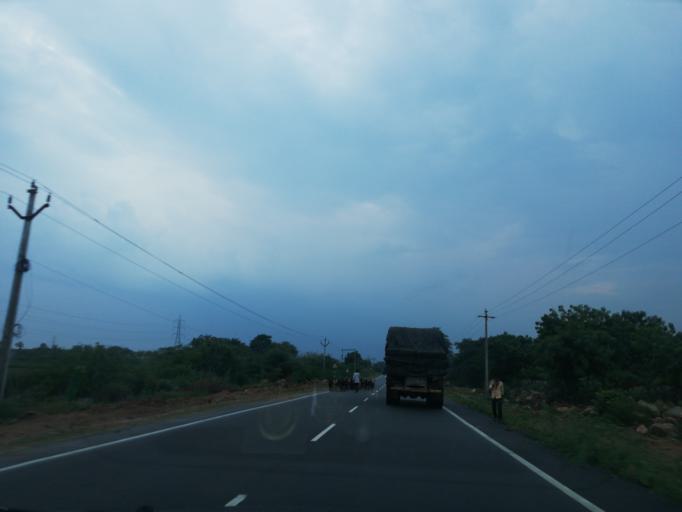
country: IN
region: Andhra Pradesh
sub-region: Guntur
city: Macherla
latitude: 16.6749
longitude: 79.2695
